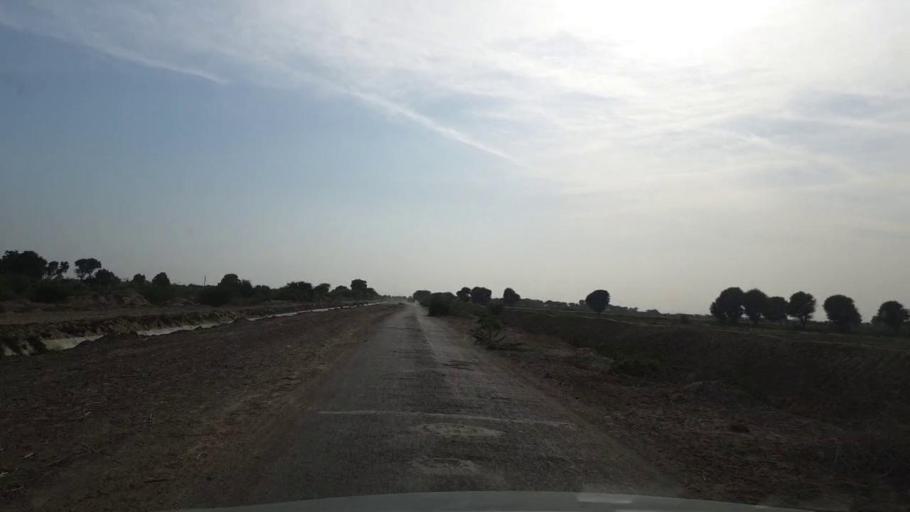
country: PK
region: Sindh
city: Kunri
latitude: 25.1554
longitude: 69.5117
